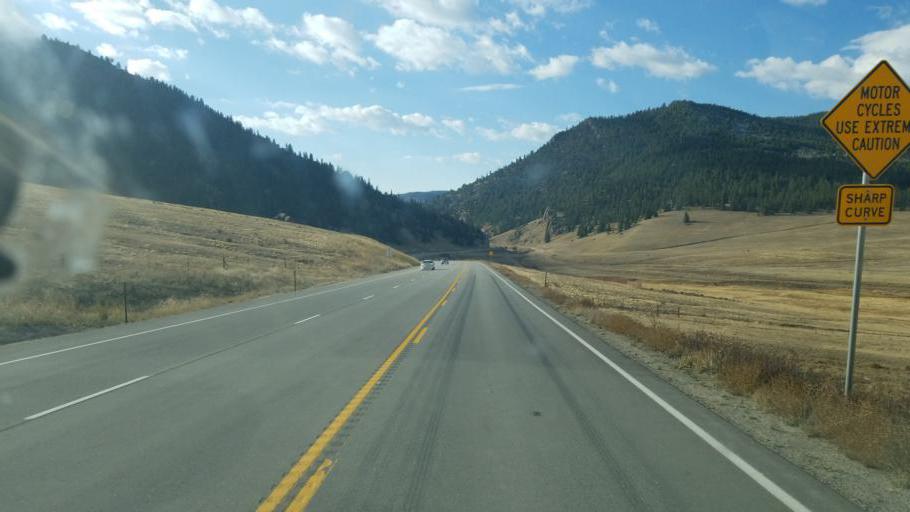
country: US
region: Colorado
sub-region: Chaffee County
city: Buena Vista
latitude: 38.8682
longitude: -105.9848
